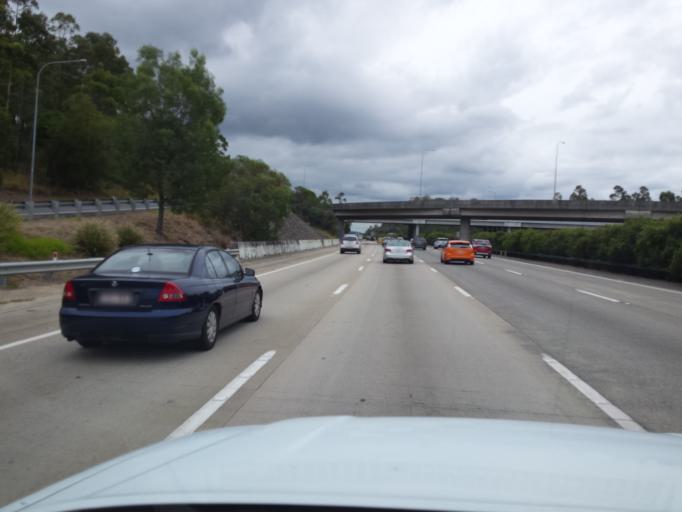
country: AU
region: Queensland
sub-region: Gold Coast
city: Oxenford
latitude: -27.9281
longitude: 153.3310
